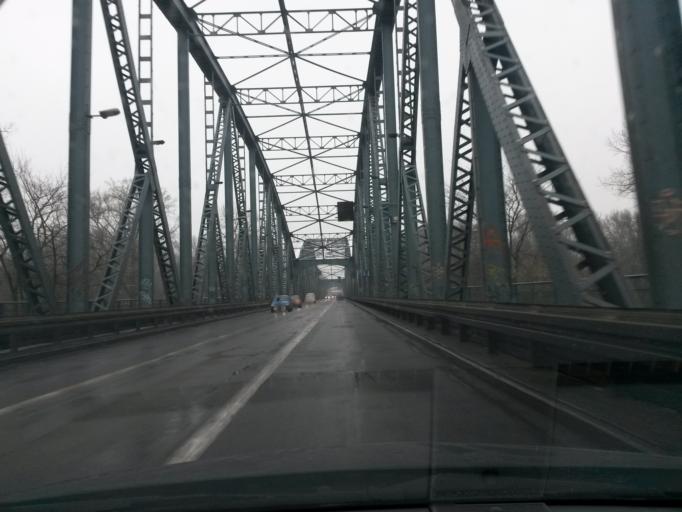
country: PL
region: Kujawsko-Pomorskie
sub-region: Torun
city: Torun
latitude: 53.0034
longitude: 18.6028
